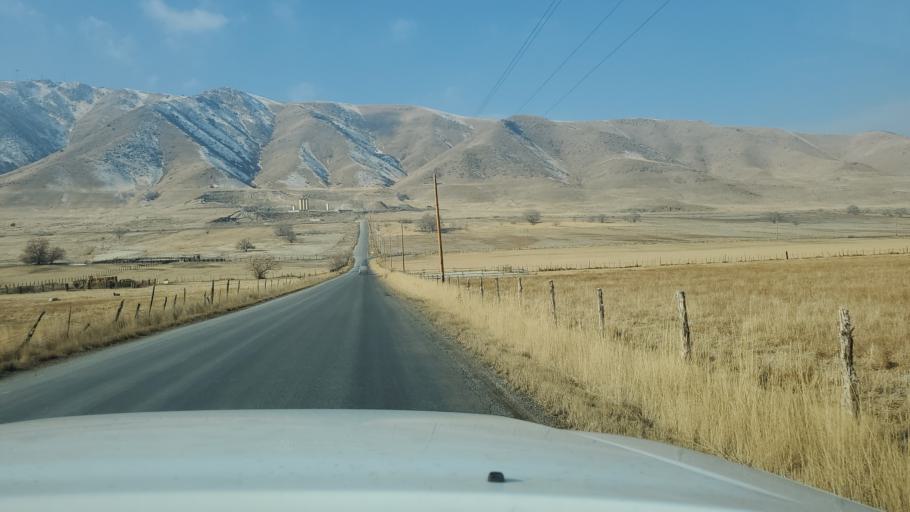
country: US
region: Utah
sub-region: Utah County
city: West Mountain
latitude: 40.0997
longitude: -111.7927
